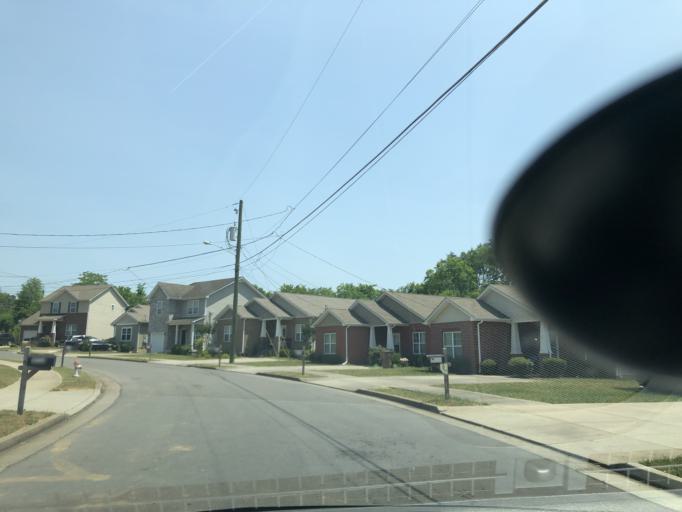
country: US
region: Tennessee
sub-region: Rutherford County
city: La Vergne
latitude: 36.0613
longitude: -86.6093
